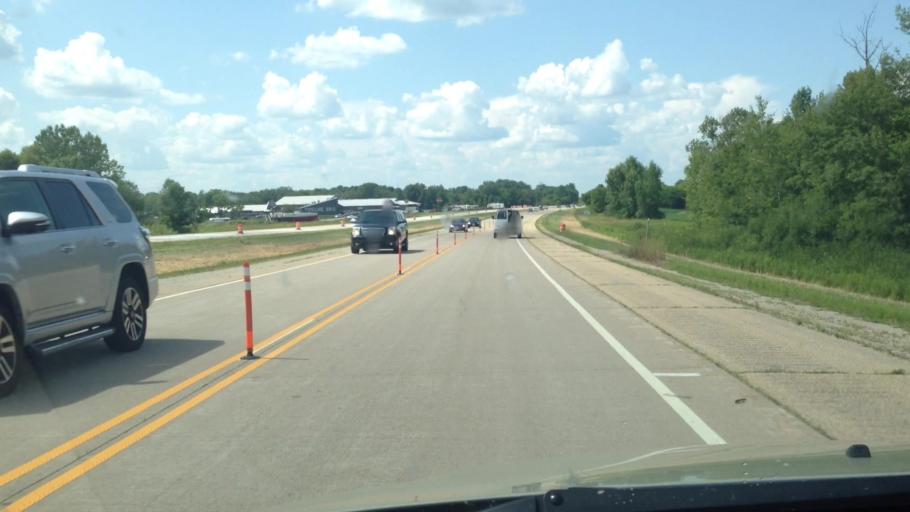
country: US
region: Wisconsin
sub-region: Shawano County
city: Bonduel
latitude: 44.7028
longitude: -88.3684
